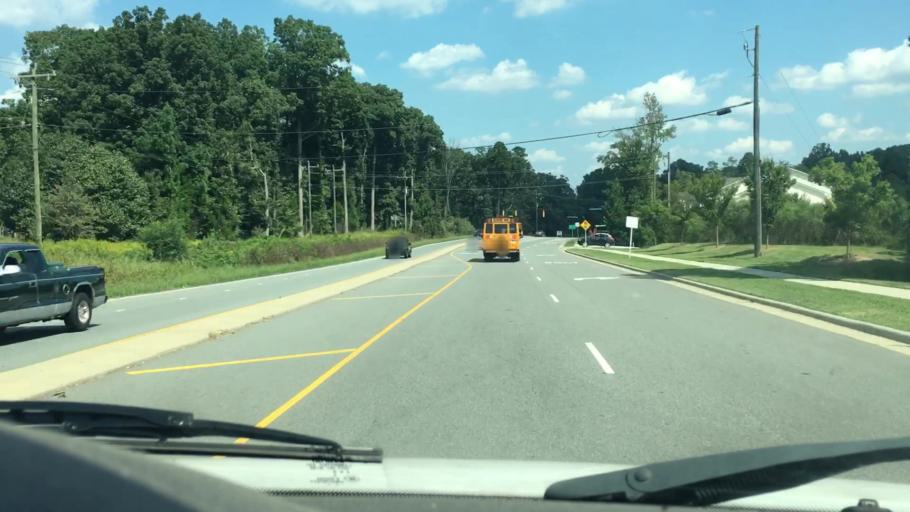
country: US
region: North Carolina
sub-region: Mecklenburg County
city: Huntersville
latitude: 35.3658
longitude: -80.8582
